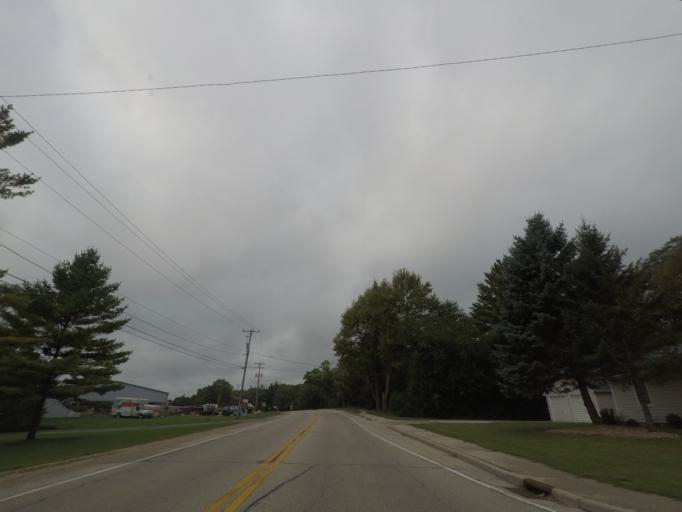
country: US
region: Wisconsin
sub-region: Waukesha County
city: Dousman
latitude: 43.0182
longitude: -88.5816
